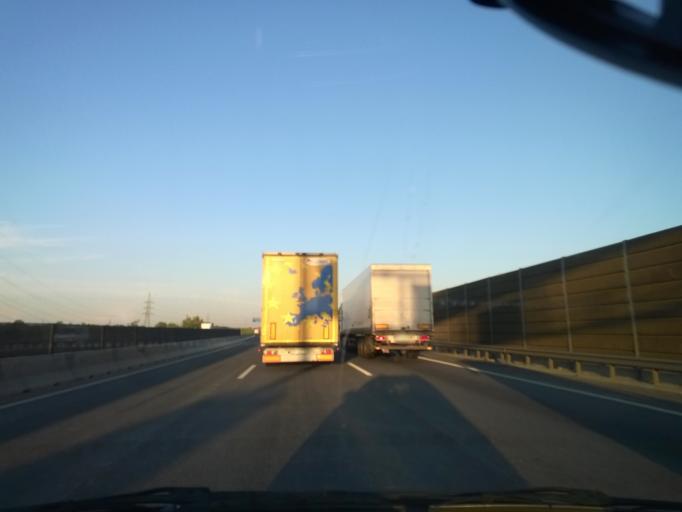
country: HU
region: Pest
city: Dunaharaszti
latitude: 47.3679
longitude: 19.1037
